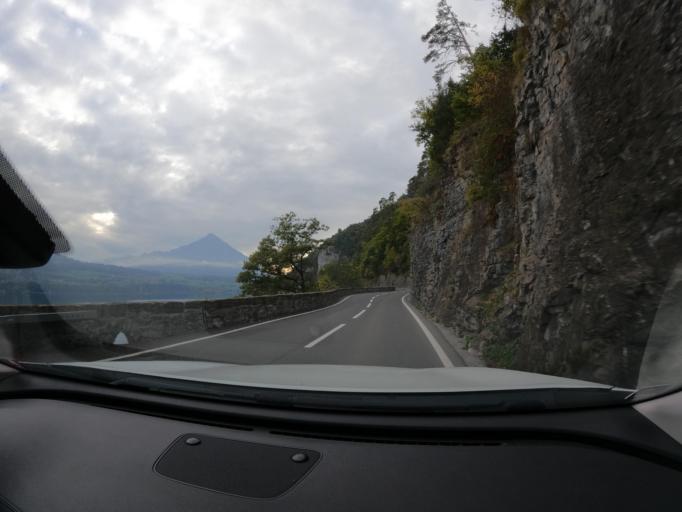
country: CH
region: Bern
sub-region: Interlaken-Oberhasli District
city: Beatenberg
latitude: 46.6827
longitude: 7.7698
